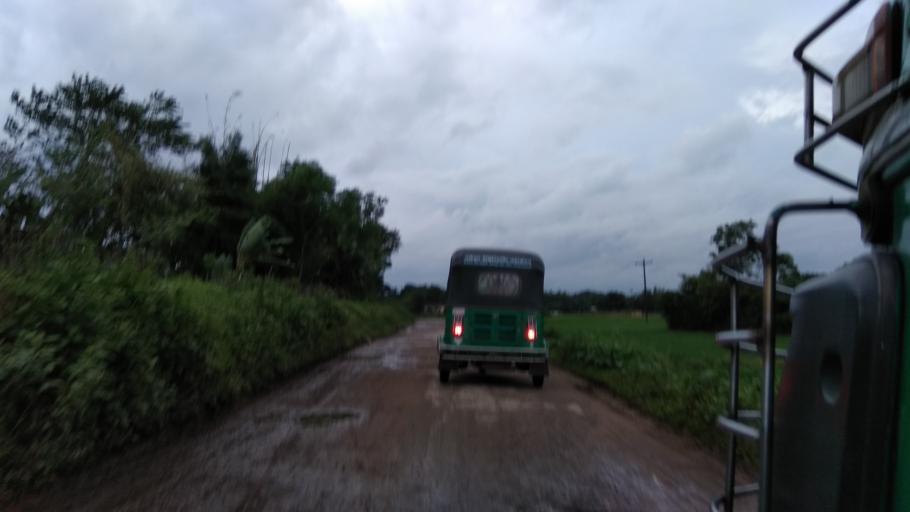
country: IN
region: Tripura
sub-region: Dhalai
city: Kamalpur
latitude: 24.2114
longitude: 91.8594
